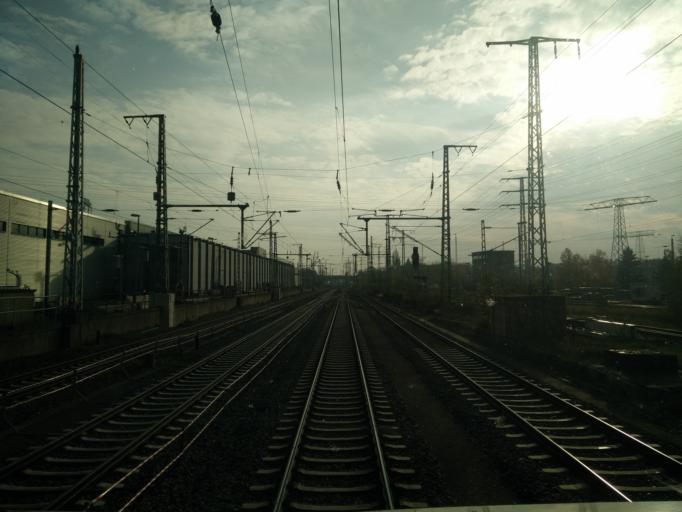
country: DE
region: Berlin
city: Friedrichsfelde
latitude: 52.4877
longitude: 13.5102
